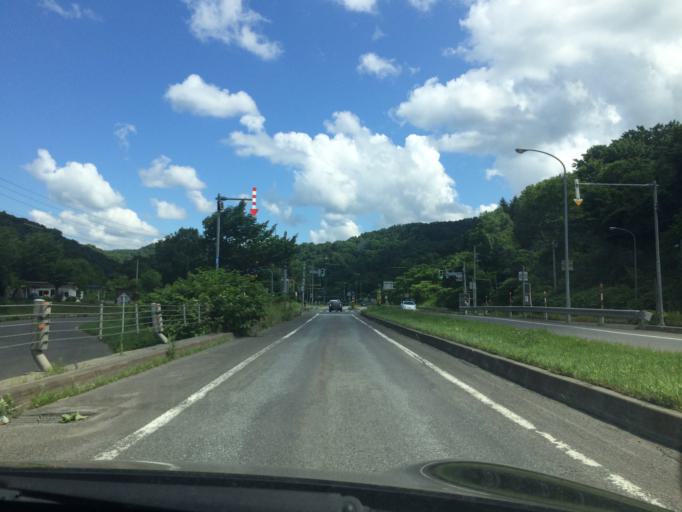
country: JP
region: Hokkaido
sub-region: Asahikawa-shi
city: Asahikawa
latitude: 43.7285
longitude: 142.2058
